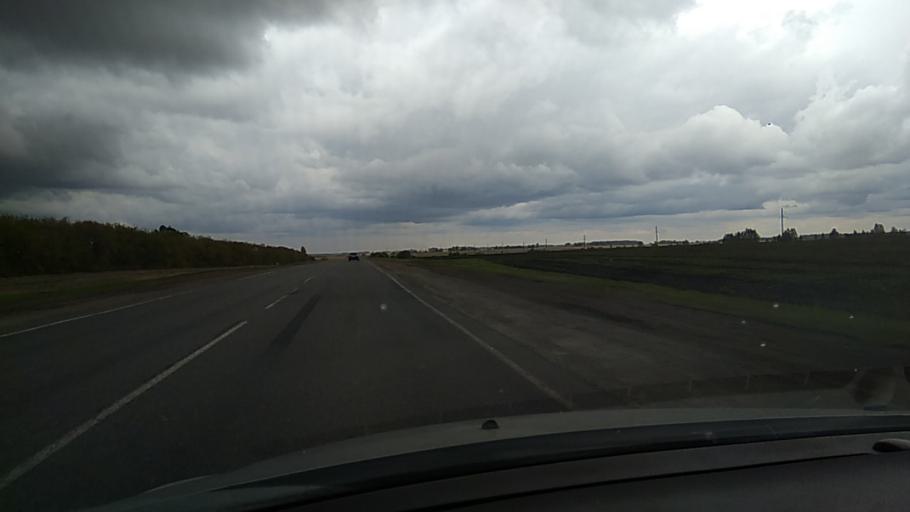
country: RU
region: Kurgan
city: Dalmatovo
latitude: 56.2897
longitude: 62.8203
